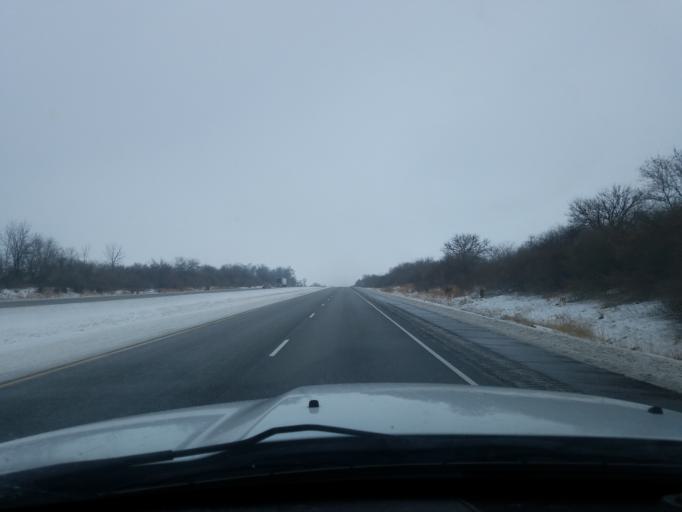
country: US
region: Indiana
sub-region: Fulton County
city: Rochester
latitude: 40.9668
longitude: -86.1681
